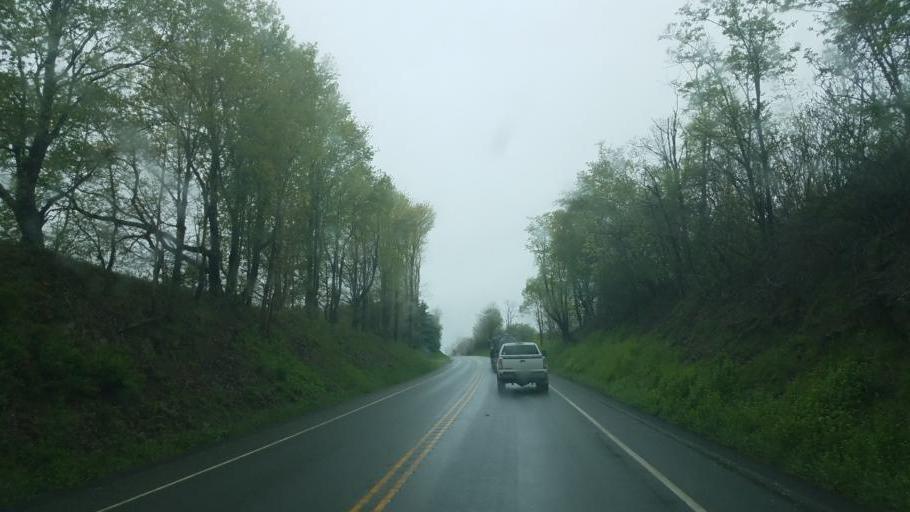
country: US
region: Pennsylvania
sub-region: McKean County
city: Port Allegany
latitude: 41.8264
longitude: -78.3465
